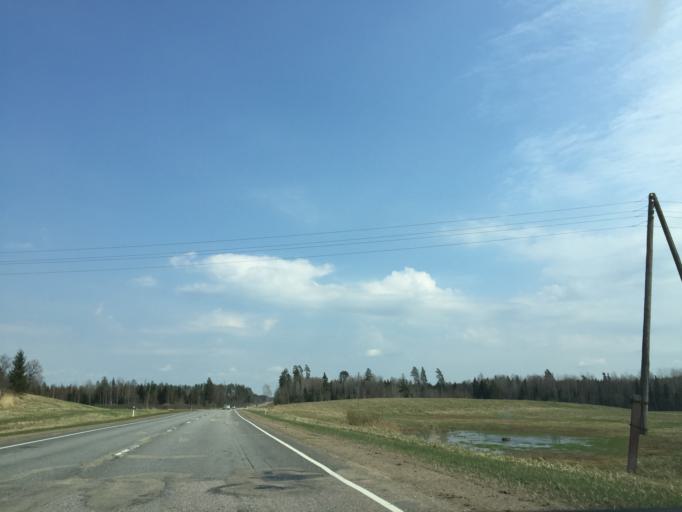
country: LV
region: Apes Novads
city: Ape
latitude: 57.4966
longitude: 26.5876
